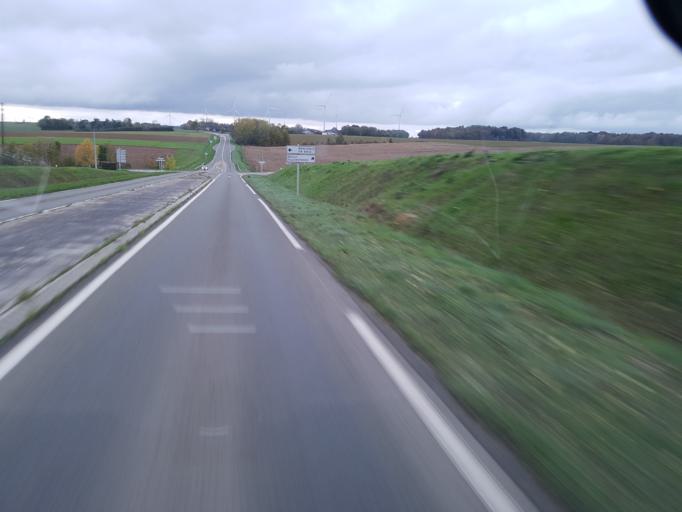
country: FR
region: Champagne-Ardenne
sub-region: Departement de la Marne
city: Montmirail
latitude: 48.8914
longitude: 3.4908
